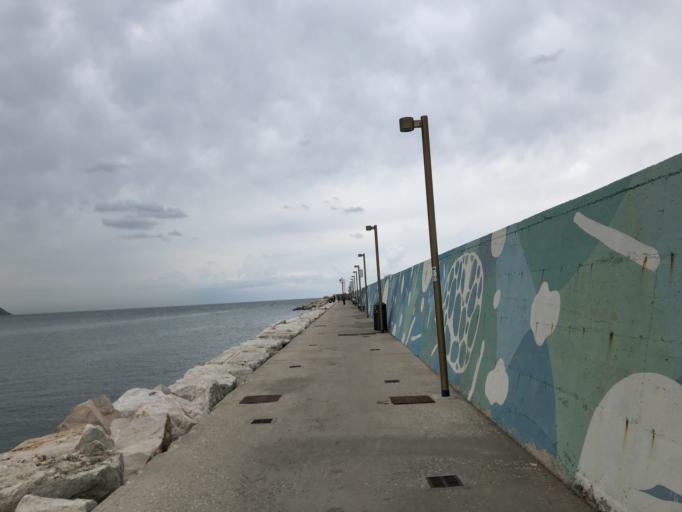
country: IT
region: The Marches
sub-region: Provincia di Pesaro e Urbino
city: Pesaro
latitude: 43.9262
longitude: 12.9070
